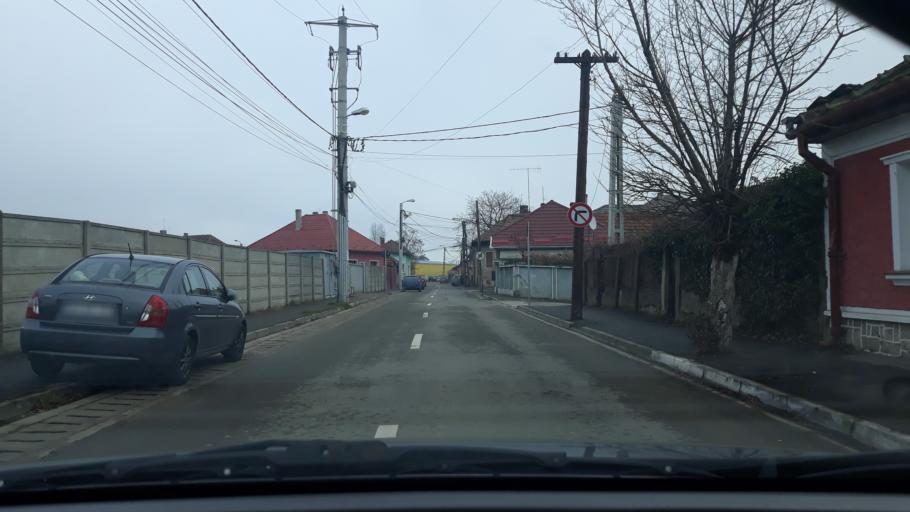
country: RO
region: Bihor
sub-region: Comuna Sanmartin
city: Sanmartin
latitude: 47.0465
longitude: 21.9712
